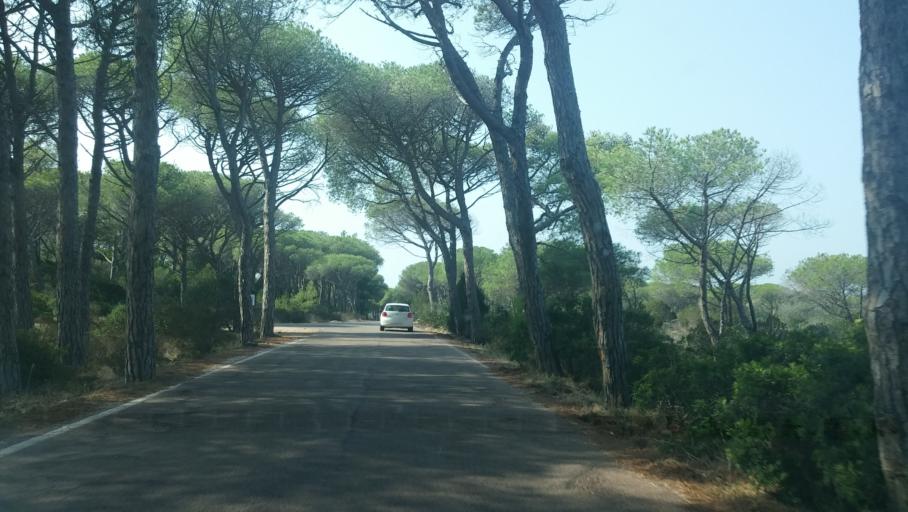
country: IT
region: Sardinia
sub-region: Provincia di Olbia-Tempio
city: La Maddalena
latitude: 41.2090
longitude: 9.4618
